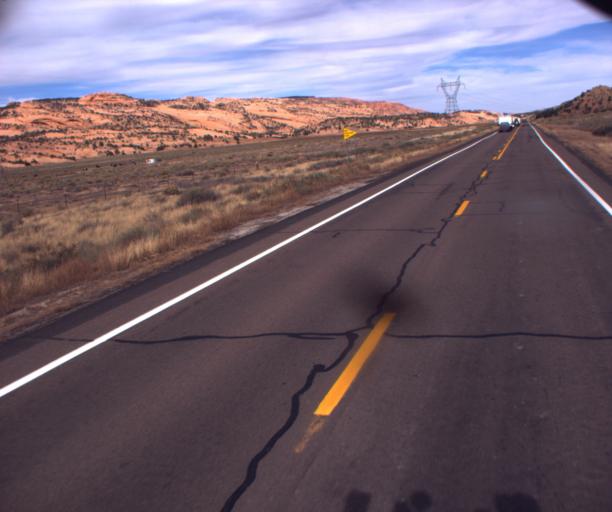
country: US
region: Arizona
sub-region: Navajo County
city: Kayenta
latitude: 36.6207
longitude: -110.4639
